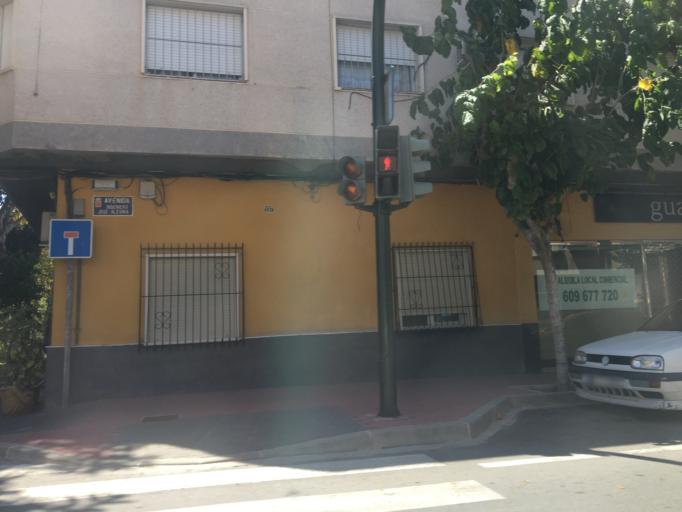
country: ES
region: Murcia
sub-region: Murcia
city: Murcia
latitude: 38.0045
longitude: -1.1152
